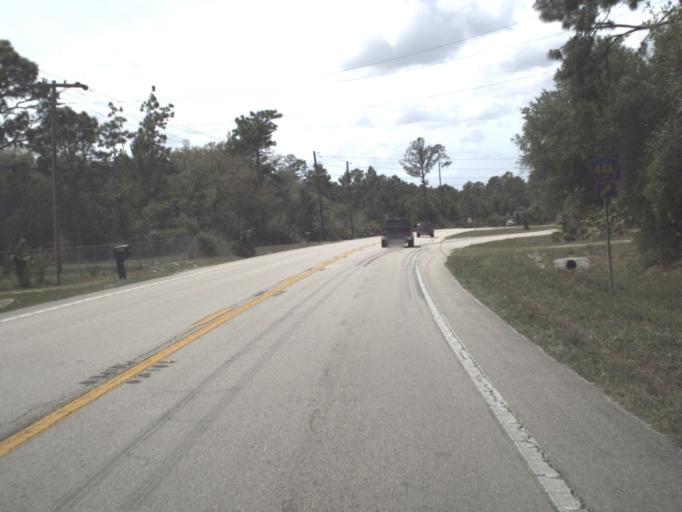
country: US
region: Florida
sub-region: Lake County
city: Mount Plymouth
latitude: 28.8780
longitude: -81.4844
